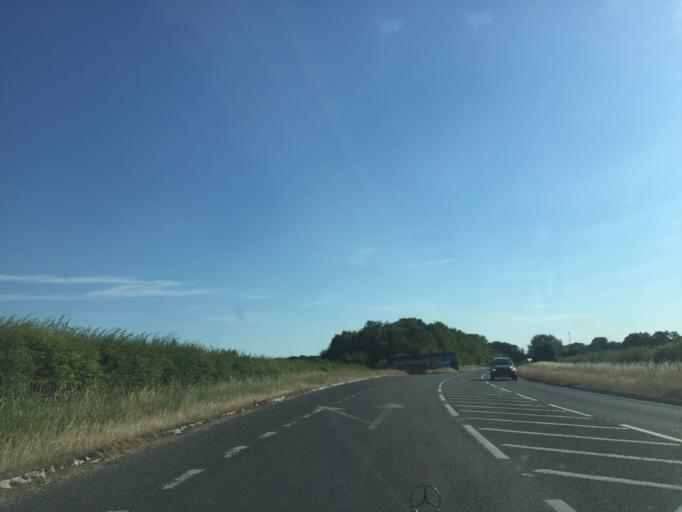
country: GB
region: England
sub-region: Oxfordshire
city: Chinnor
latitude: 51.6747
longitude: -0.9548
